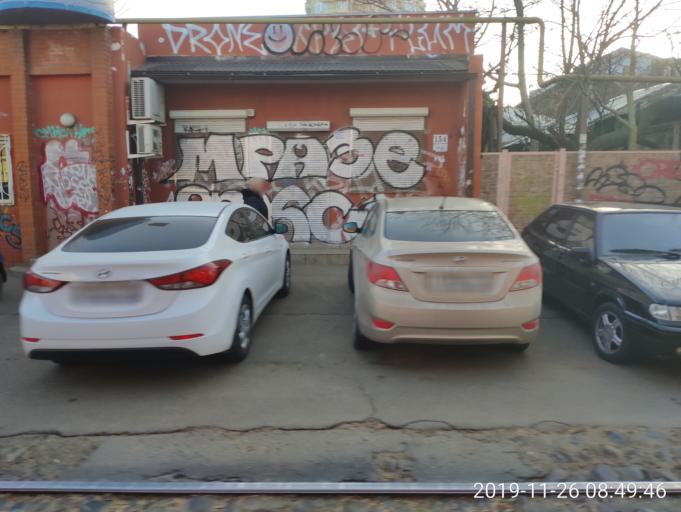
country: RU
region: Krasnodarskiy
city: Krasnodar
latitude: 45.0330
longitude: 38.9776
